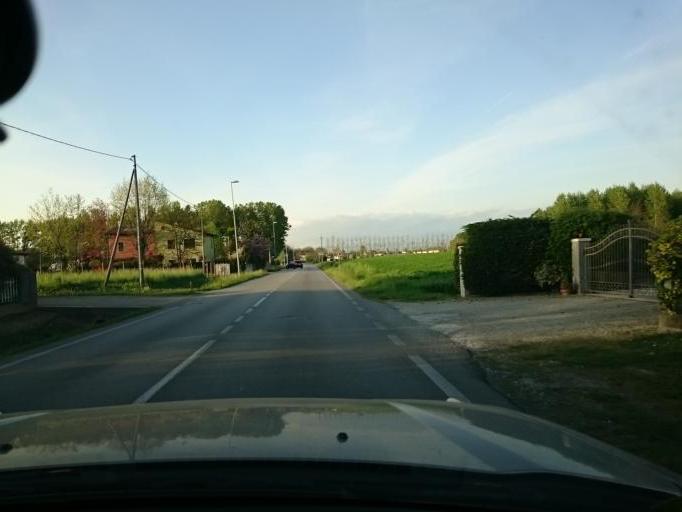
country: IT
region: Veneto
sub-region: Provincia di Treviso
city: Badoere
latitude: 45.6436
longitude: 12.1048
